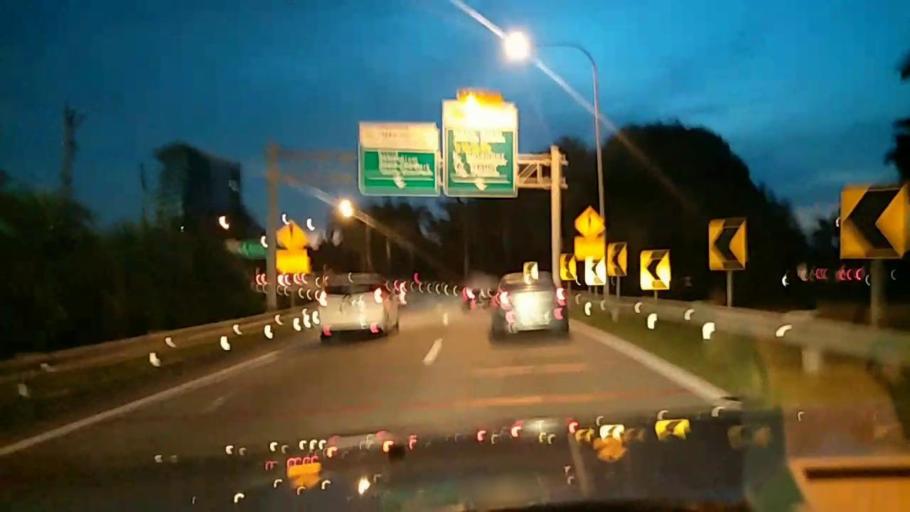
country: MY
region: Selangor
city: Shah Alam
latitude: 3.0905
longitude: 101.5488
